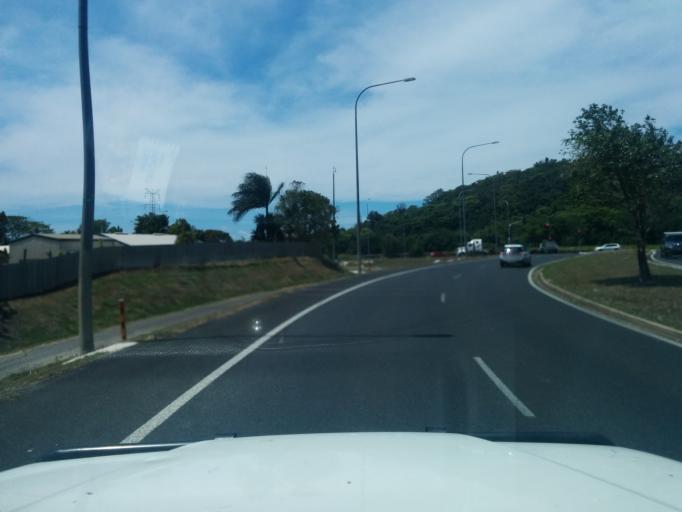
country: AU
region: Queensland
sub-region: Cairns
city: Redlynch
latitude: -16.8919
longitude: 145.7006
